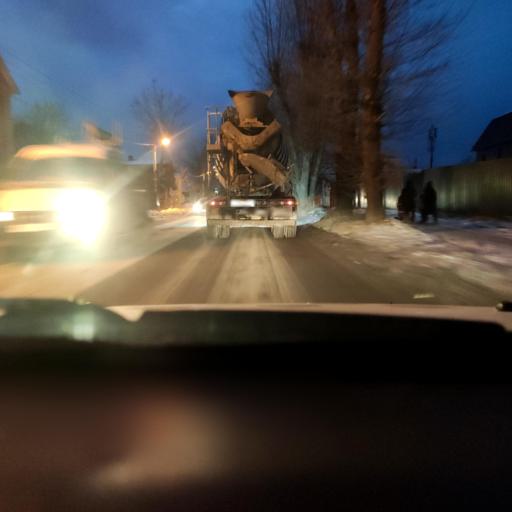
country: RU
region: Perm
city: Perm
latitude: 58.0366
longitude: 56.3351
